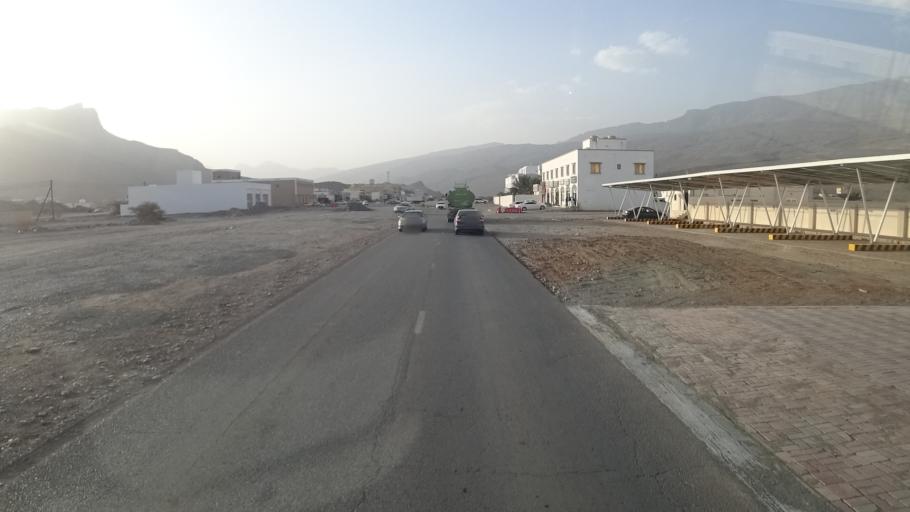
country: OM
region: Muhafazat ad Dakhiliyah
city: Bahla'
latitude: 23.1119
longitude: 57.2678
